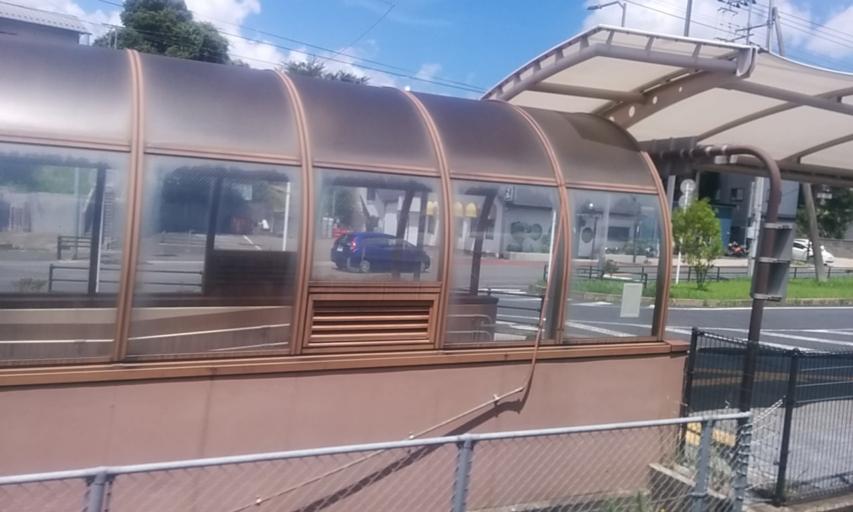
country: JP
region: Chiba
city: Oami
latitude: 35.5314
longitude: 140.2685
